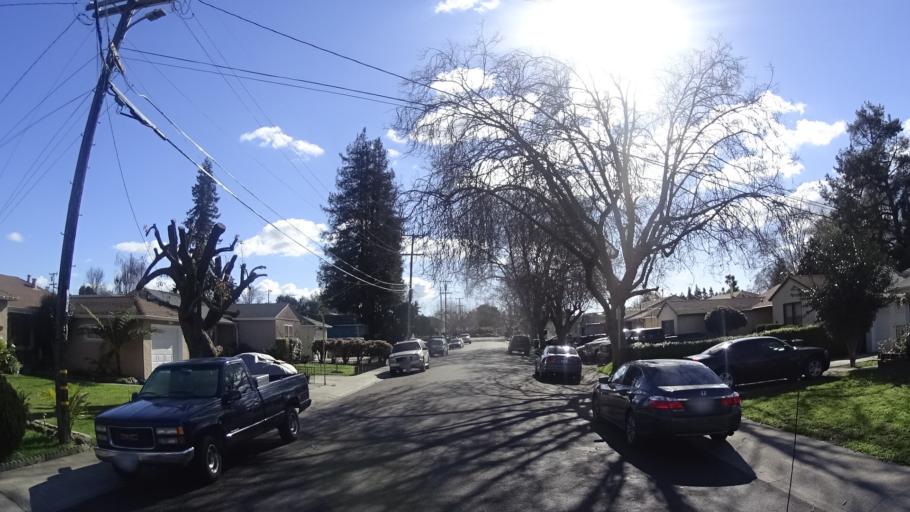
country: US
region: California
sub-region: Alameda County
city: Ashland
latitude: 37.6883
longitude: -122.1160
